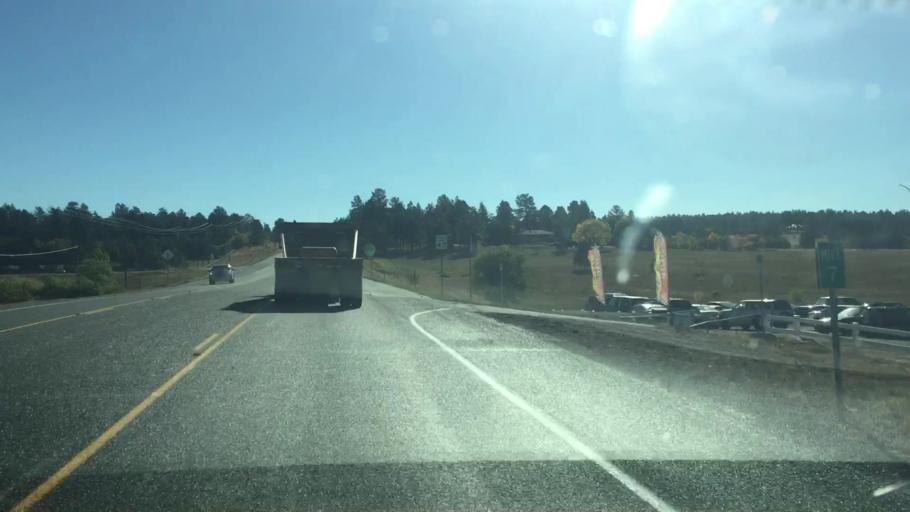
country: US
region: Colorado
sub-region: Douglas County
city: The Pinery
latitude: 39.3903
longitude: -104.7493
